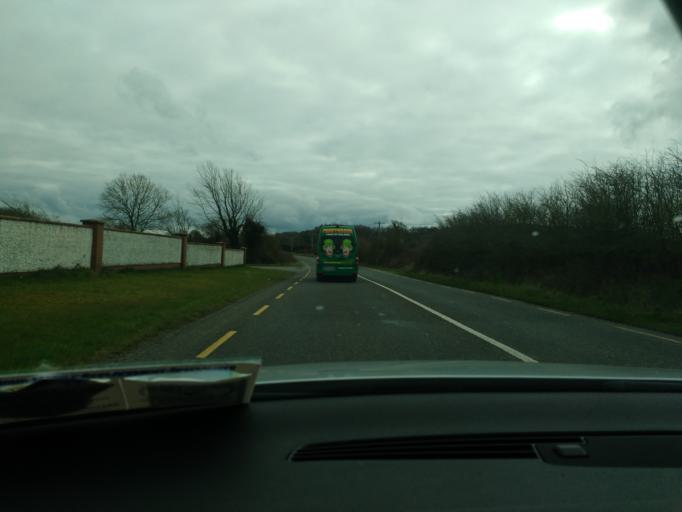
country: IE
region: Leinster
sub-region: Kilkenny
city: Ballyragget
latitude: 52.7280
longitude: -7.3776
